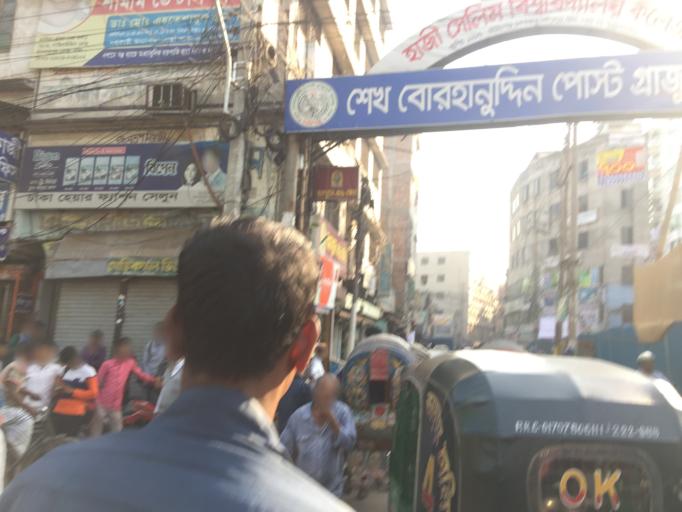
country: BD
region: Dhaka
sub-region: Dhaka
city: Dhaka
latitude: 23.7239
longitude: 90.4004
